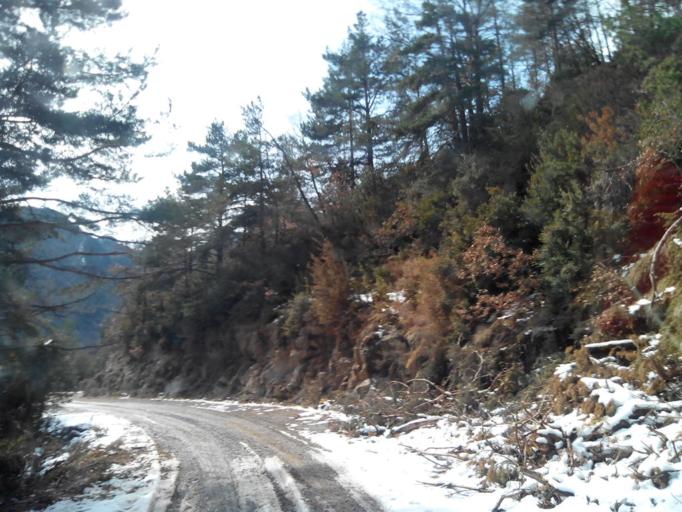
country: ES
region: Catalonia
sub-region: Provincia de Barcelona
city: Vilada
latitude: 42.1843
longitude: 1.9349
